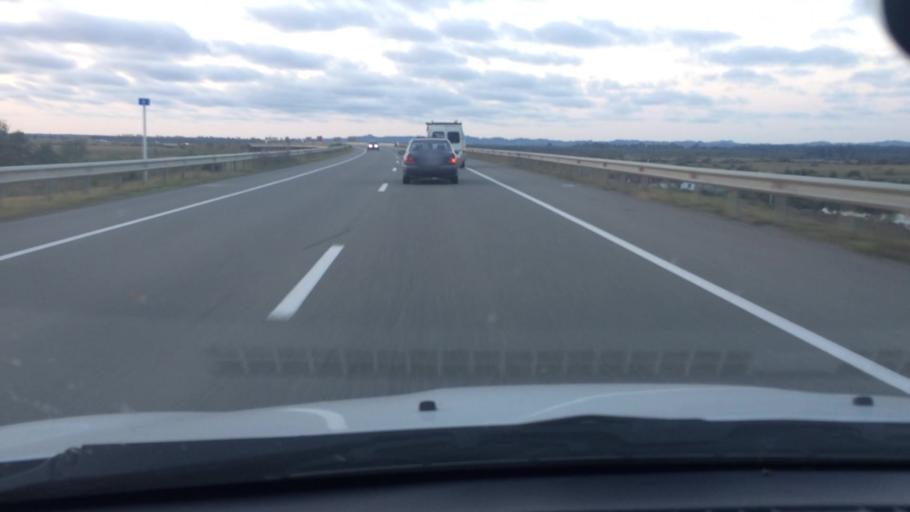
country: GE
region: Ajaria
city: Ochkhamuri
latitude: 41.8635
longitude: 41.8374
